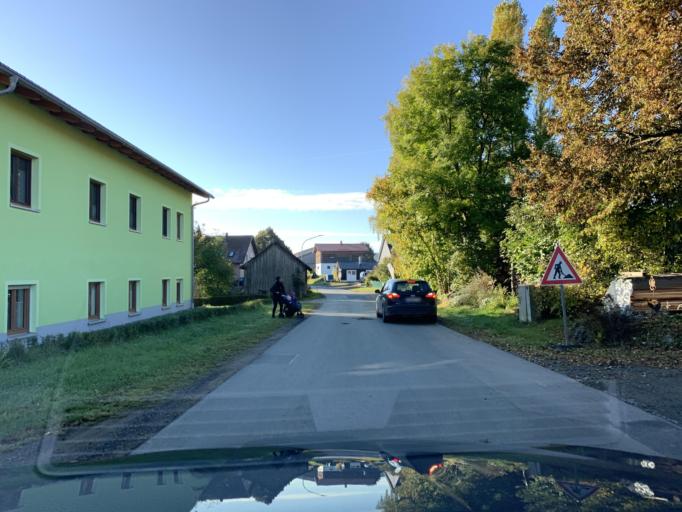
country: DE
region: Bavaria
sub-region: Upper Palatinate
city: Thanstein
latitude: 49.4038
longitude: 12.4634
